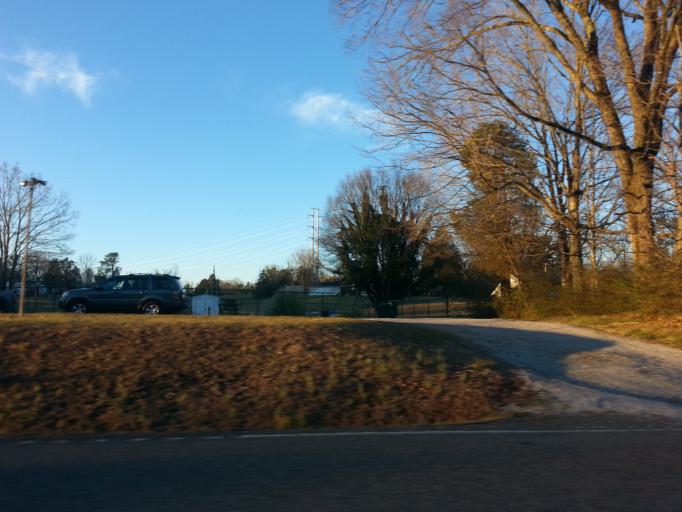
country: US
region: Tennessee
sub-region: Knox County
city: Mascot
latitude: 36.0190
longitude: -83.7489
